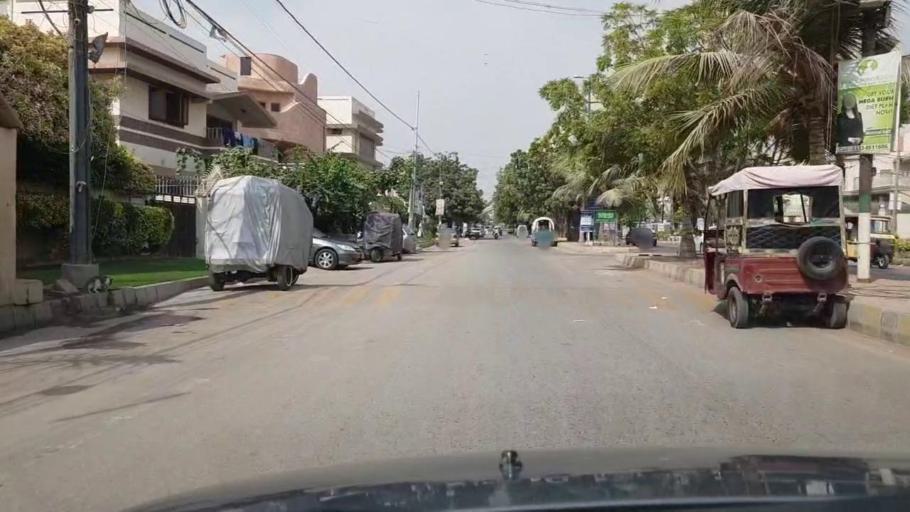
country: PK
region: Sindh
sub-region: Karachi District
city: Karachi
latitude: 24.8746
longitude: 67.0862
